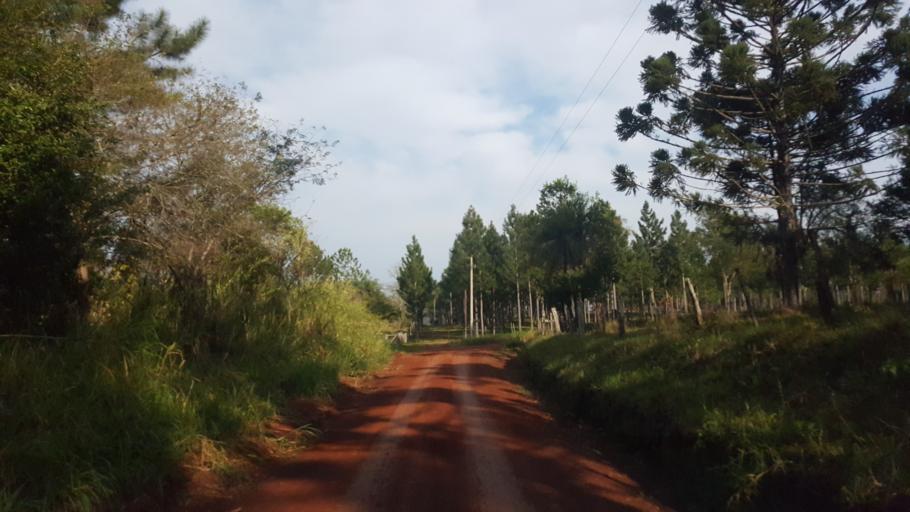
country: AR
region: Misiones
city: Capiovi
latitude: -26.8940
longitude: -55.1065
